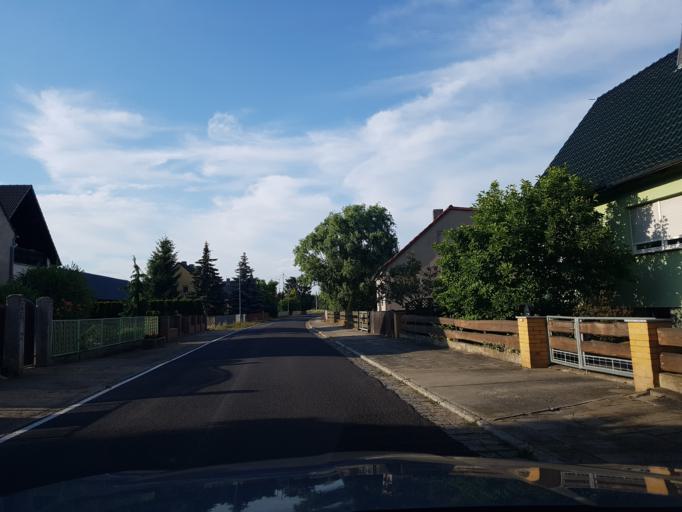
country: DE
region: Brandenburg
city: Falkenberg
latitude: 51.5521
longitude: 13.2935
